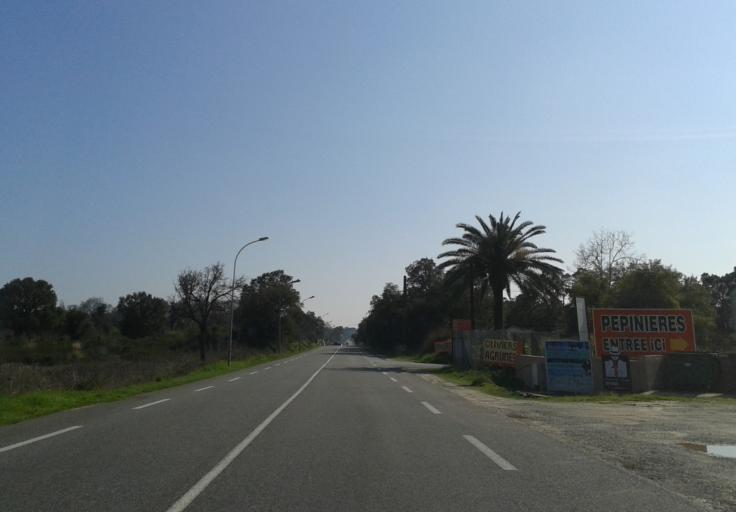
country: FR
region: Corsica
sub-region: Departement de la Haute-Corse
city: Linguizzetta
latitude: 42.2139
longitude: 9.5336
